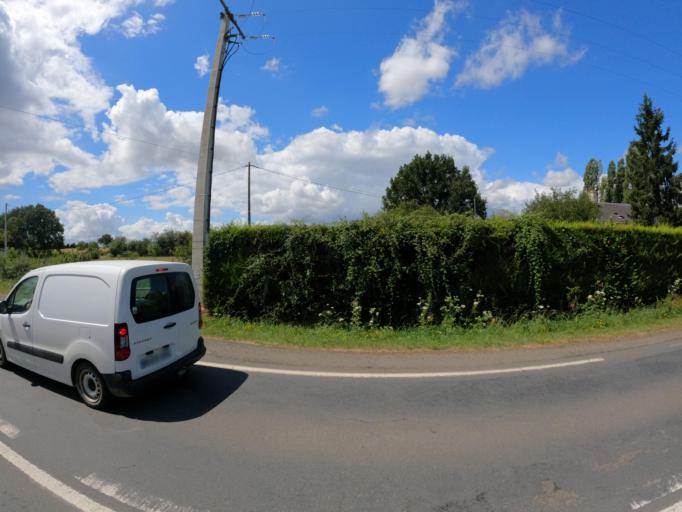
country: FR
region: Pays de la Loire
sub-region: Departement de la Sarthe
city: Juigne-sur-Sarthe
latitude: 47.9142
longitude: -0.2702
